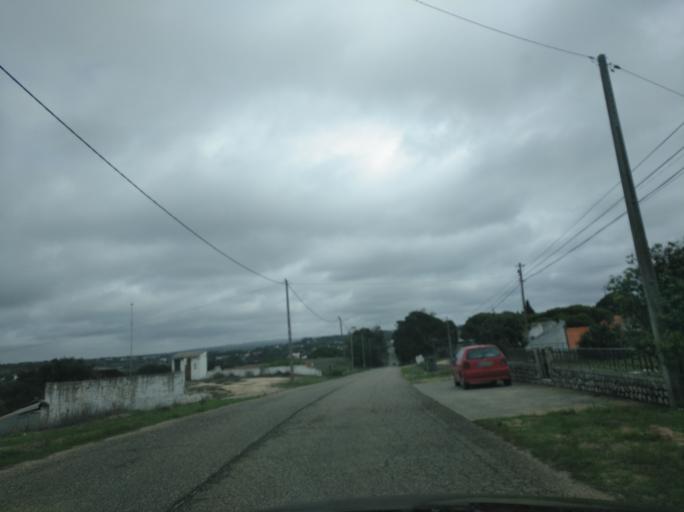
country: PT
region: Setubal
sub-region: Santiago do Cacem
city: Santo Andre
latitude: 38.1385
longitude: -8.7484
